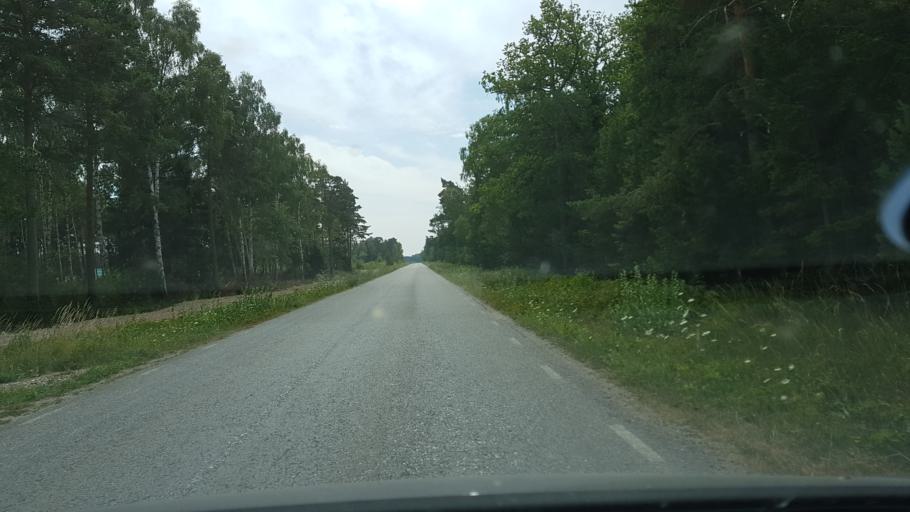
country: SE
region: Gotland
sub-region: Gotland
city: Visby
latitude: 57.7140
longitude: 18.5084
